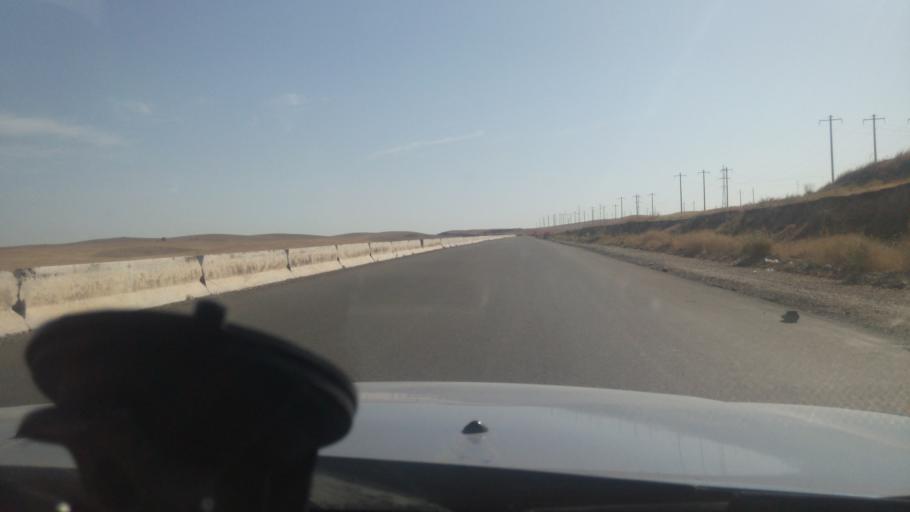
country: UZ
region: Jizzax
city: Jizzax
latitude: 40.0435
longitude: 67.6642
